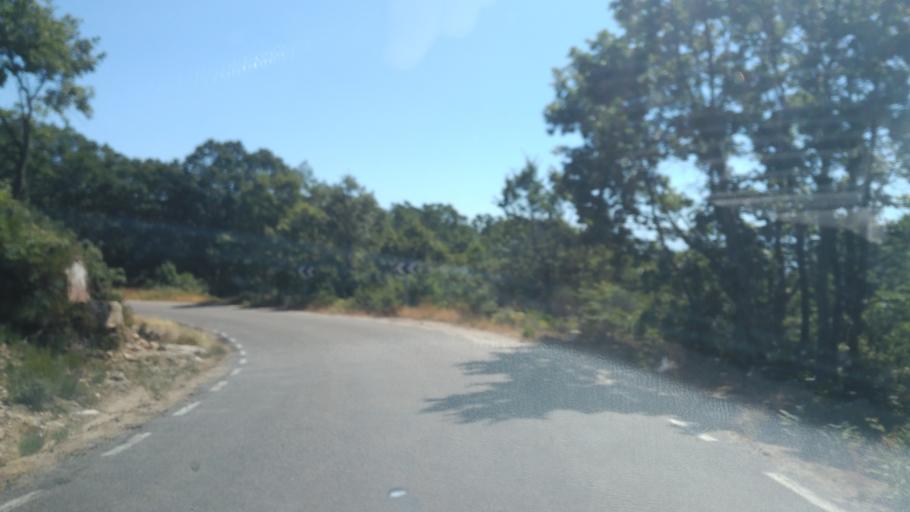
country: ES
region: Castille and Leon
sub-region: Provincia de Salamanca
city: San Martin del Castanar
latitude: 40.5248
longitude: -6.0790
